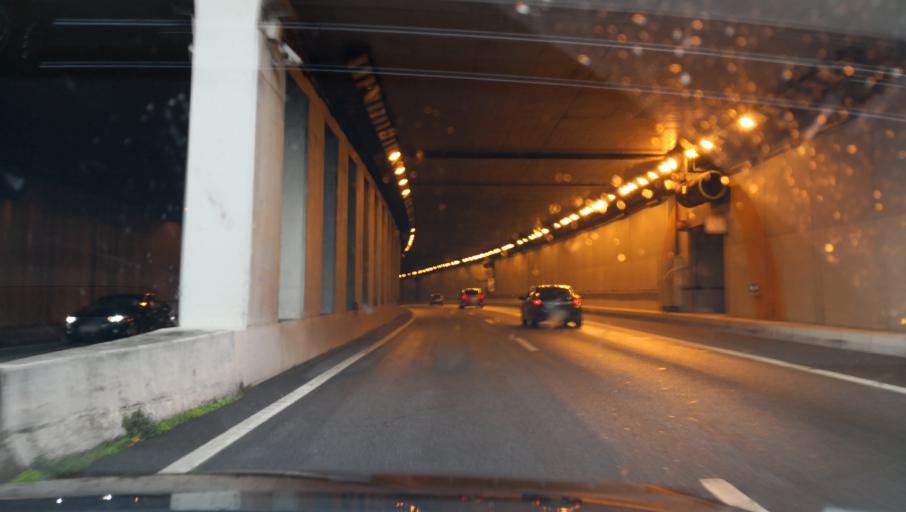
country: PT
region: Porto
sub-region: Vila Nova de Gaia
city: Vila Nova de Gaia
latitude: 41.1227
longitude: -8.6147
